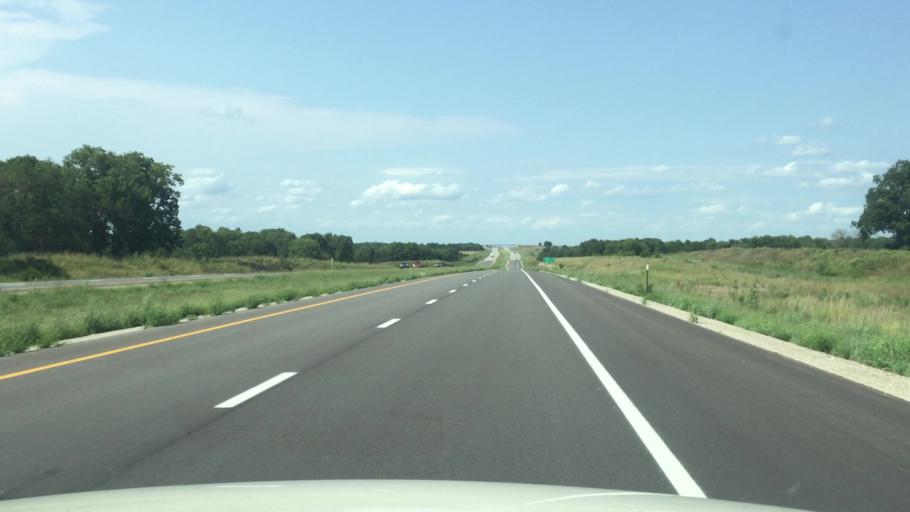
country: US
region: Kansas
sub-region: Linn County
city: La Cygne
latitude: 38.3803
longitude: -94.6874
